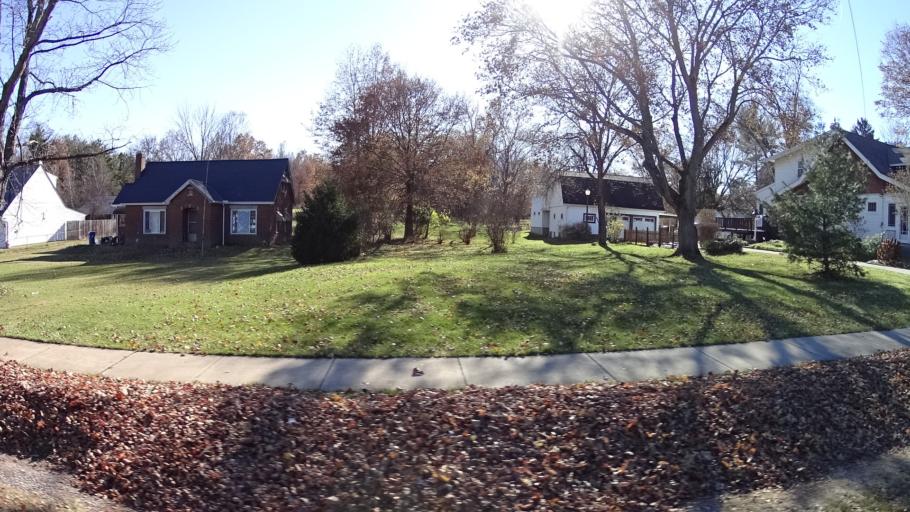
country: US
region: Ohio
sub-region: Lorain County
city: Avon Center
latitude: 41.4531
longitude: -81.9963
